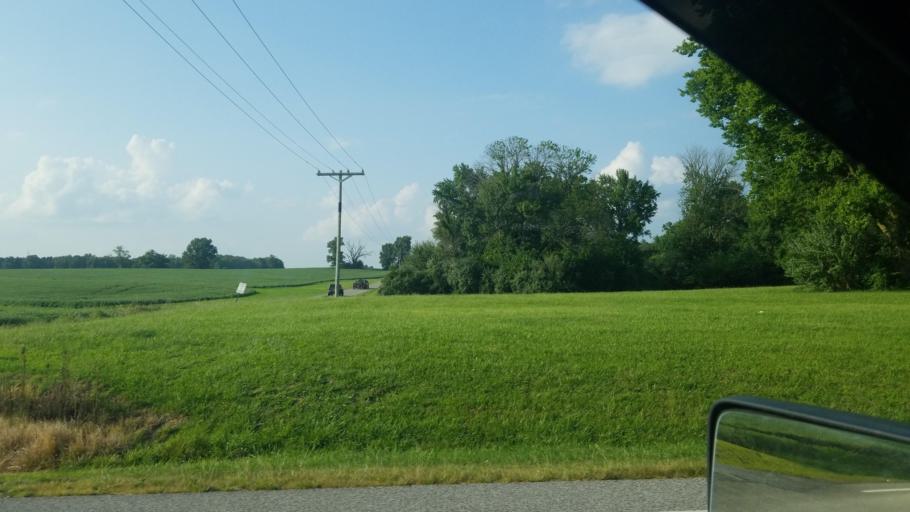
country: US
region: Illinois
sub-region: Saline County
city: Harrisburg
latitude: 37.8341
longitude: -88.5487
